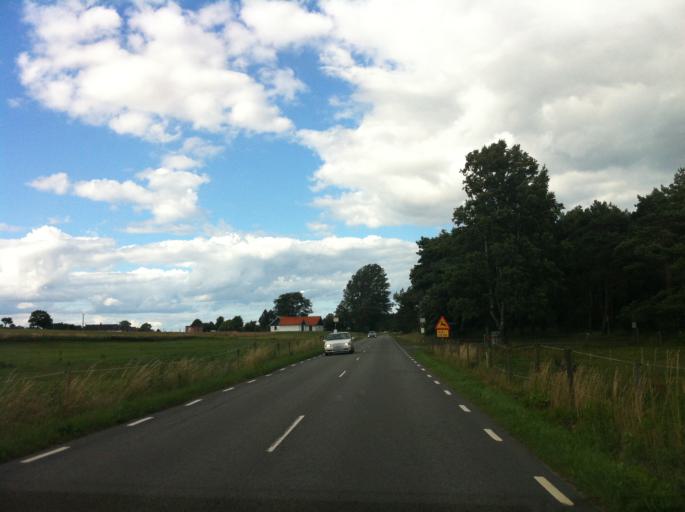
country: SE
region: Skane
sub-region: Simrishamns Kommun
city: Simrishamn
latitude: 55.4186
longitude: 14.2099
